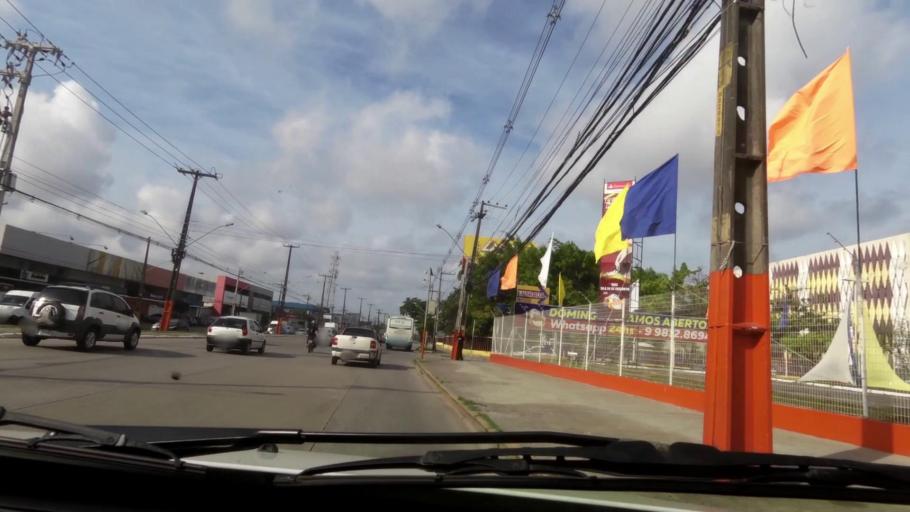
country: BR
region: Pernambuco
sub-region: Recife
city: Recife
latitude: -8.0957
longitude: -34.9095
